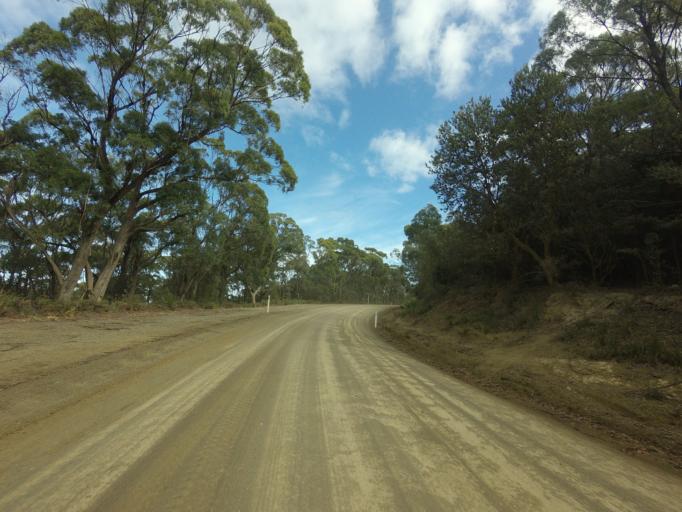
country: AU
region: Tasmania
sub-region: Clarence
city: Sandford
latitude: -43.0936
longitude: 147.7286
